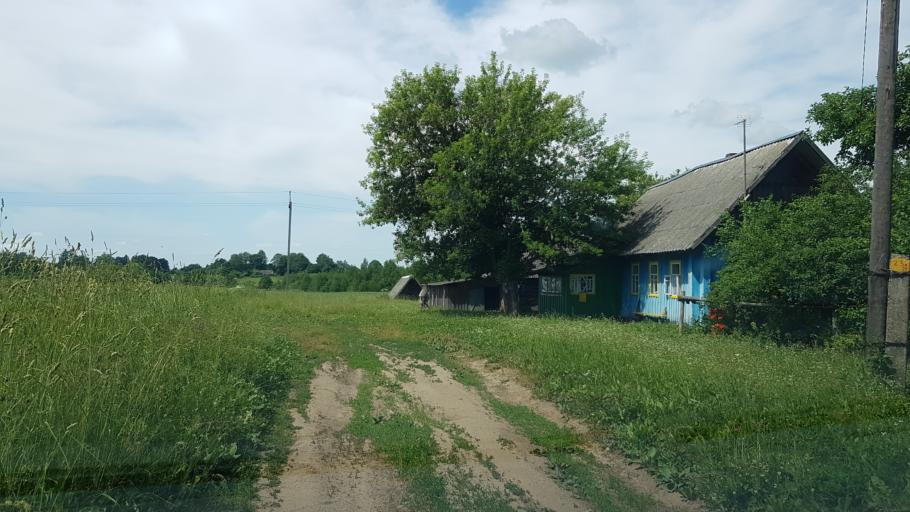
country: BY
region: Vitebsk
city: Dubrowna
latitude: 54.4886
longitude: 30.7908
